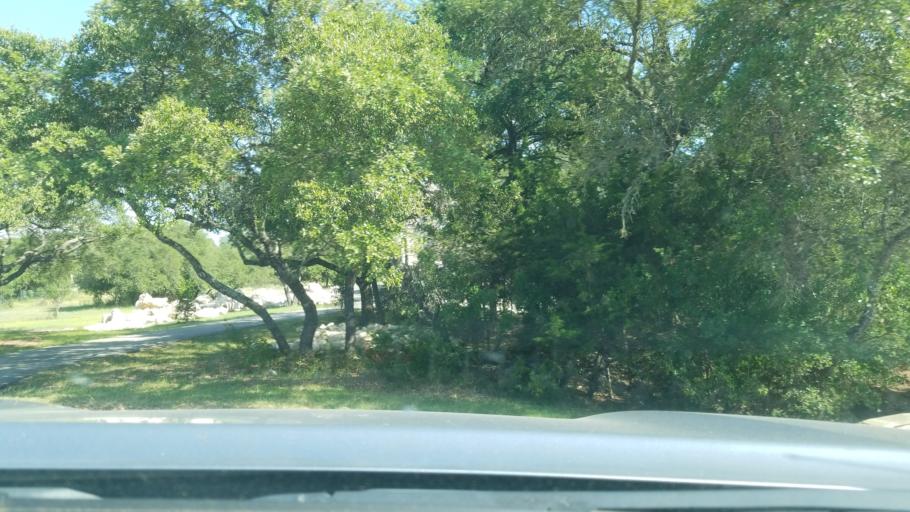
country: US
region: Texas
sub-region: Comal County
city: Bulverde
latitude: 29.8303
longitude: -98.4049
